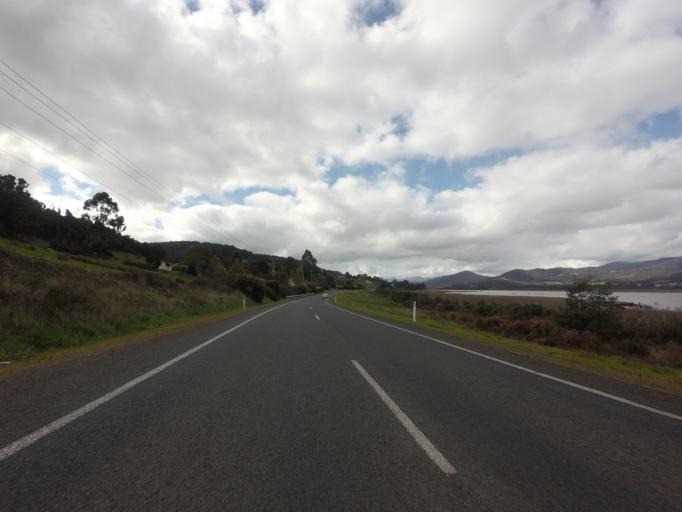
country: AU
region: Tasmania
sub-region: Huon Valley
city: Franklin
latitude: -43.1201
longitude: 146.9904
